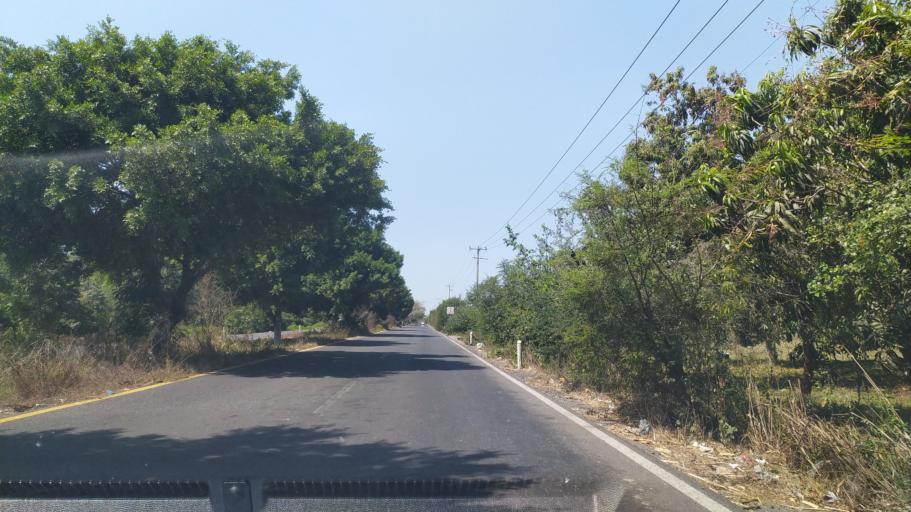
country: MX
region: Colima
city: Tecoman
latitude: 18.9364
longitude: -103.8711
